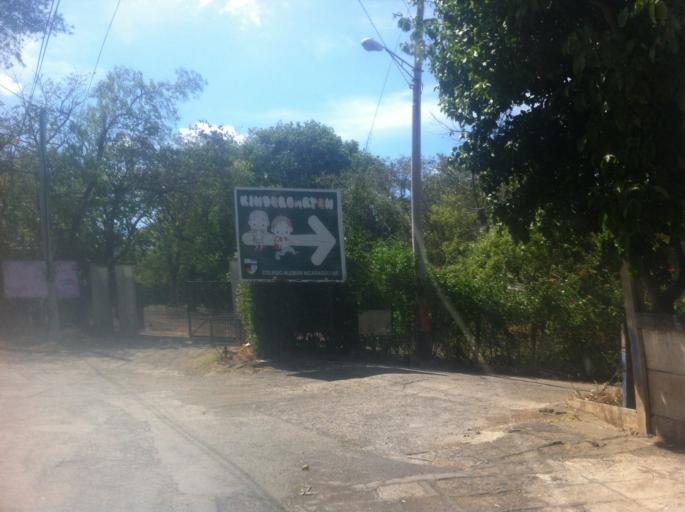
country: NI
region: Managua
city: Ciudad Sandino
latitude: 12.0883
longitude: -86.3282
